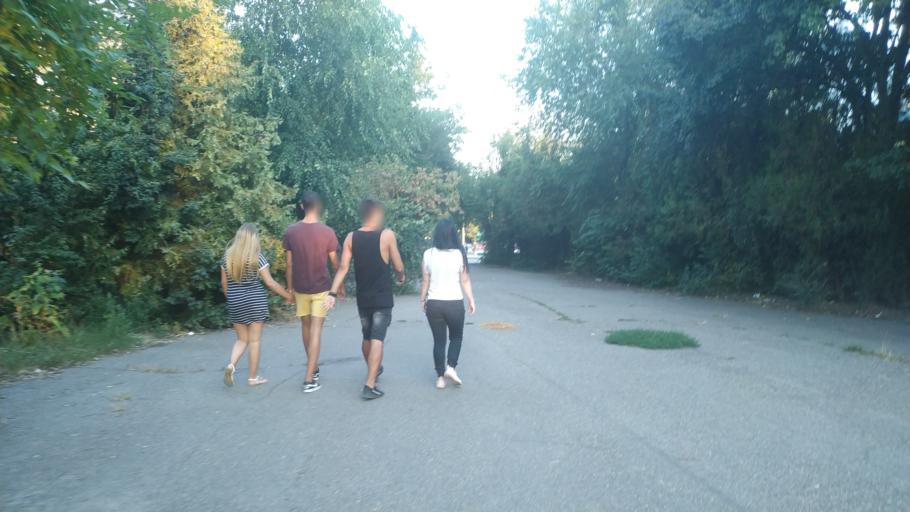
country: RO
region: Ilfov
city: Dobroesti
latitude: 44.4256
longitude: 26.1622
